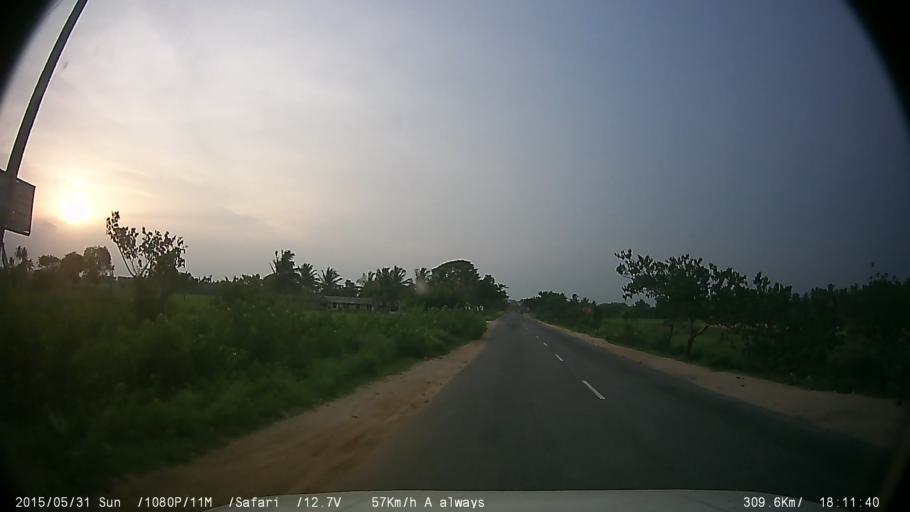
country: IN
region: Karnataka
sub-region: Mysore
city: Nanjangud
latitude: 12.0897
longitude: 76.6739
